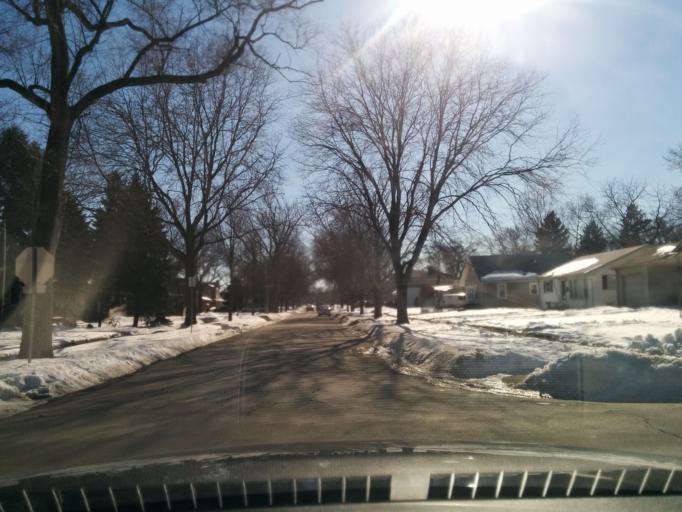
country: US
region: Illinois
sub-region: DuPage County
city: Villa Park
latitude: 41.8926
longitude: -87.9839
